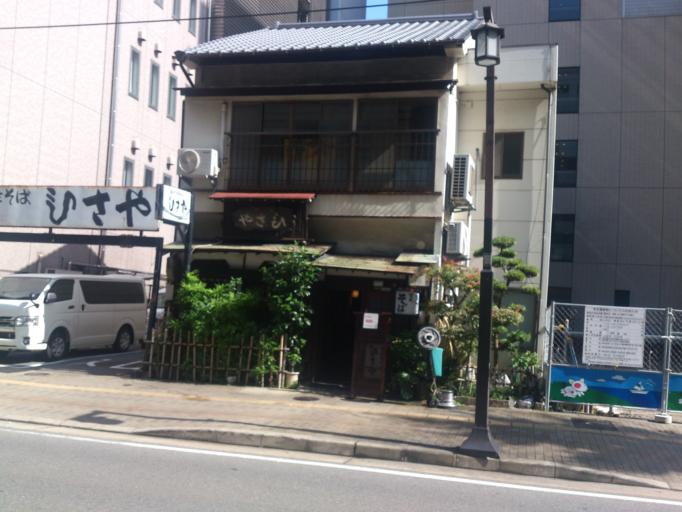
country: JP
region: Fukuoka
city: Fukuoka-shi
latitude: 33.5954
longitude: 130.4083
